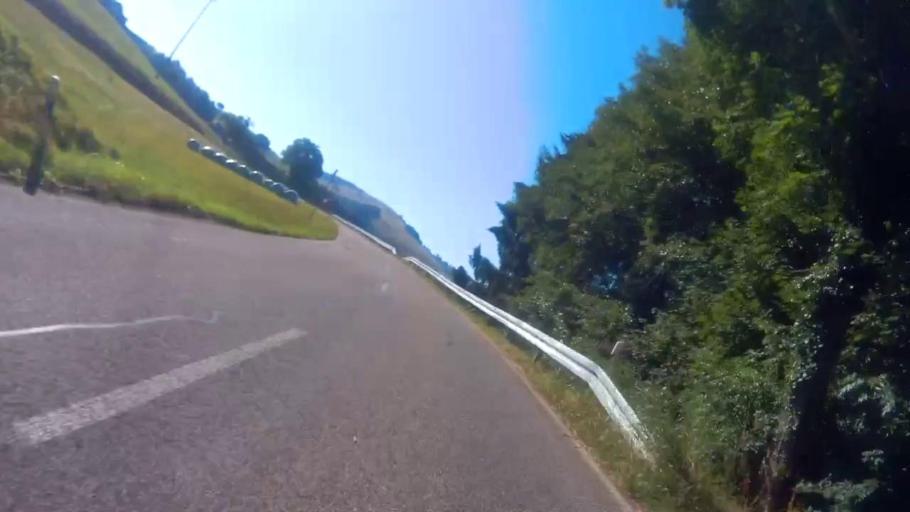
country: DE
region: Baden-Wuerttemberg
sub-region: Freiburg Region
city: Wembach
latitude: 47.7653
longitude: 7.8894
